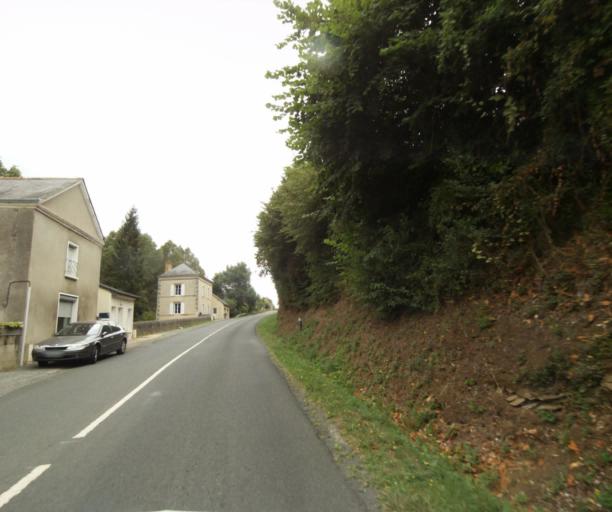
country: FR
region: Pays de la Loire
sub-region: Departement de la Sarthe
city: Juigne-sur-Sarthe
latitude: 47.8603
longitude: -0.2888
